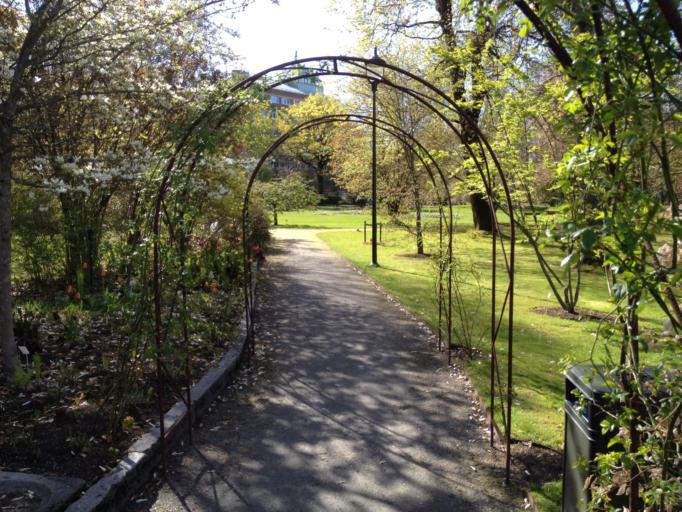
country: SE
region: Vaermland
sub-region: Karlstads Kommun
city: Karlstad
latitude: 59.3761
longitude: 13.5019
